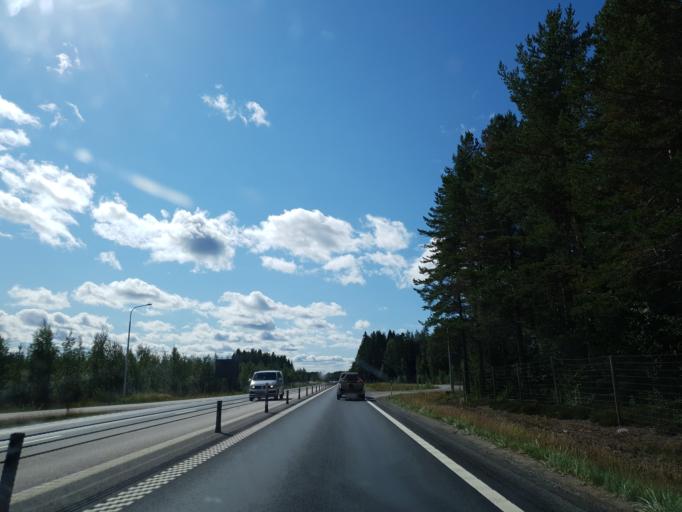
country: SE
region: Vaesterbotten
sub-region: Nordmalings Kommun
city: Nordmaling
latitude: 63.5542
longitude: 19.4201
